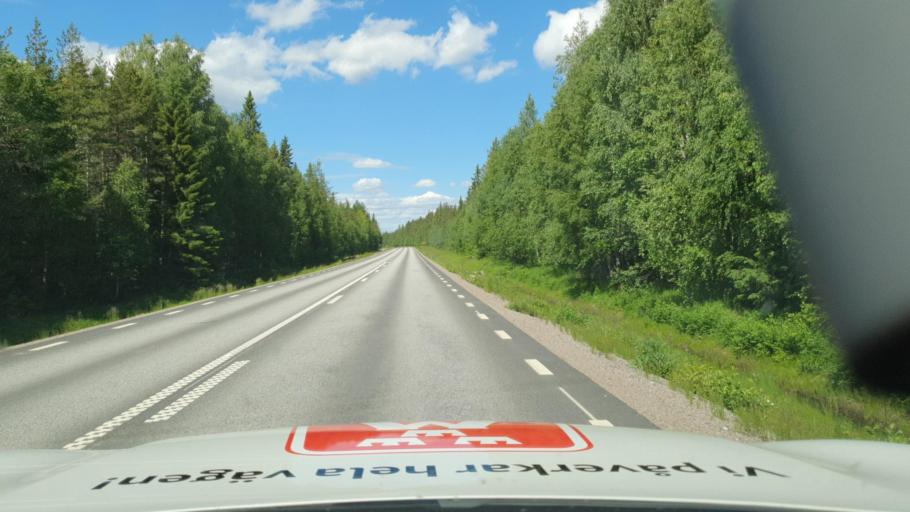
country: SE
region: Vaesterbotten
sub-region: Skelleftea Kommun
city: Boliden
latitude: 64.9111
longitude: 20.3430
